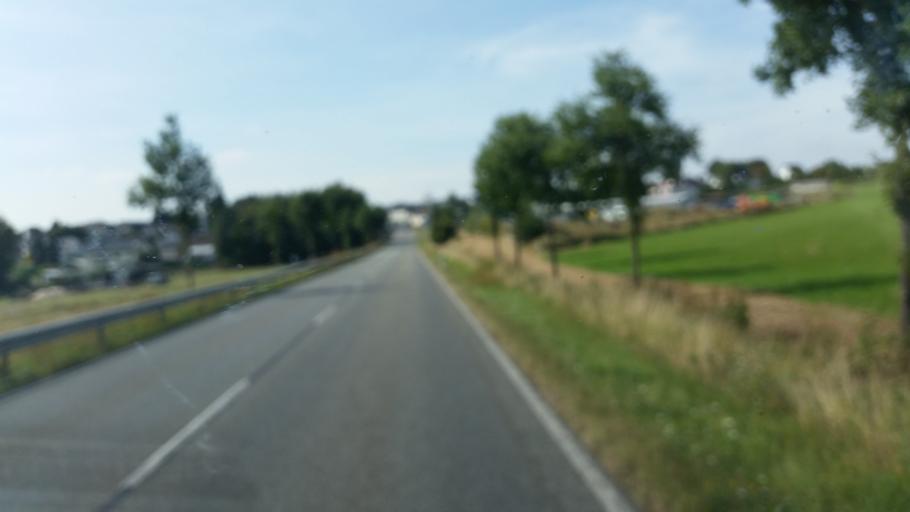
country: DE
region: Rheinland-Pfalz
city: Hohn
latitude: 50.6177
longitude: 7.9939
